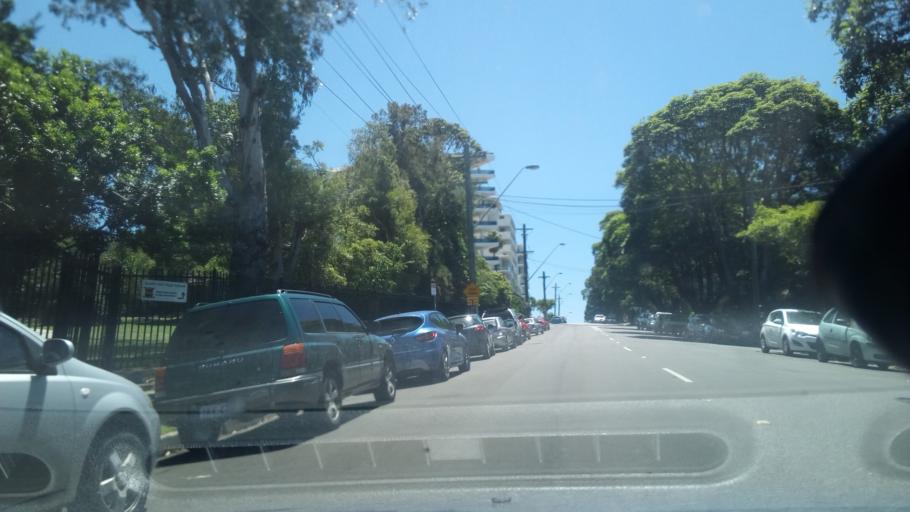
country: AU
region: New South Wales
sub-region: Wollongong
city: Wollongong
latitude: -34.4191
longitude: 150.8968
